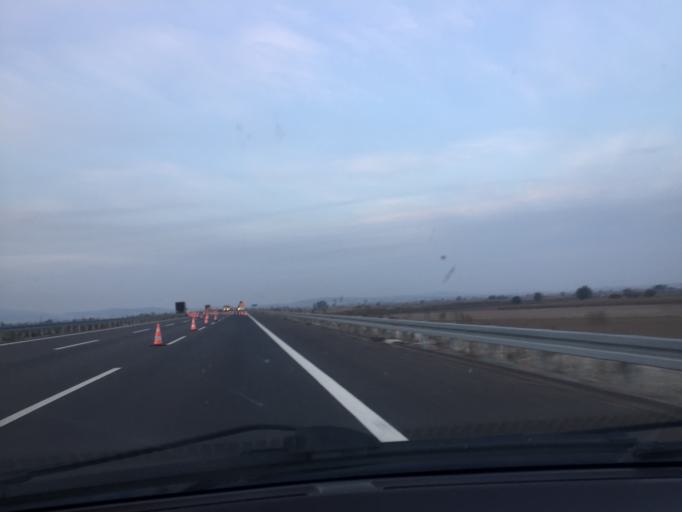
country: TR
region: Manisa
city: Halitpasa
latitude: 38.7211
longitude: 27.6519
